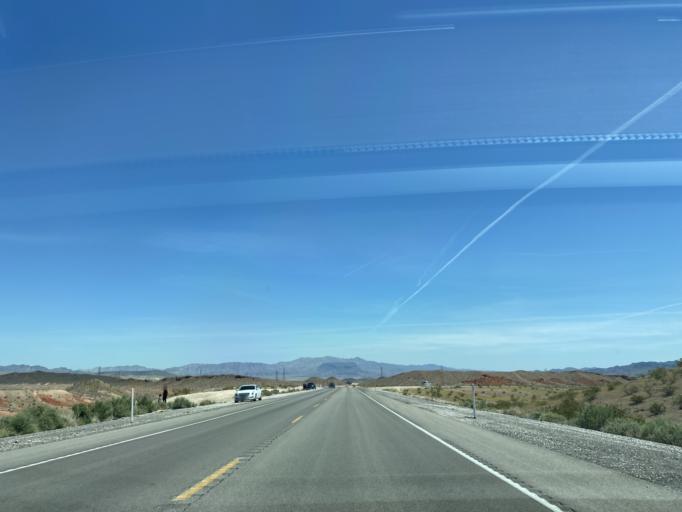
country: US
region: Nevada
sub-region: Clark County
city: Nellis Air Force Base
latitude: 36.1977
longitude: -114.9311
